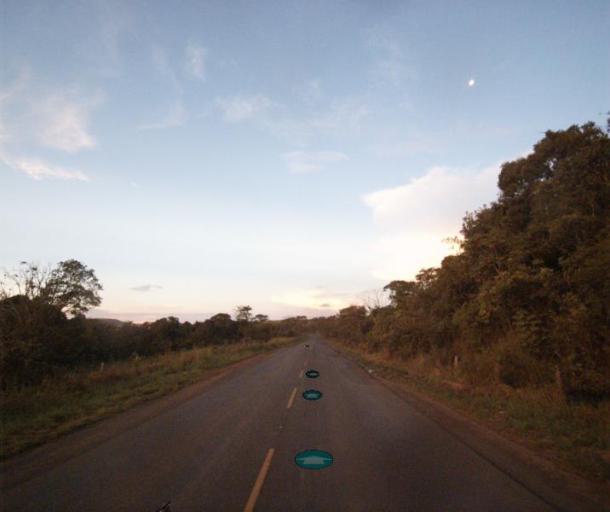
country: BR
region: Goias
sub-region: Pirenopolis
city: Pirenopolis
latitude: -15.9892
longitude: -48.8331
